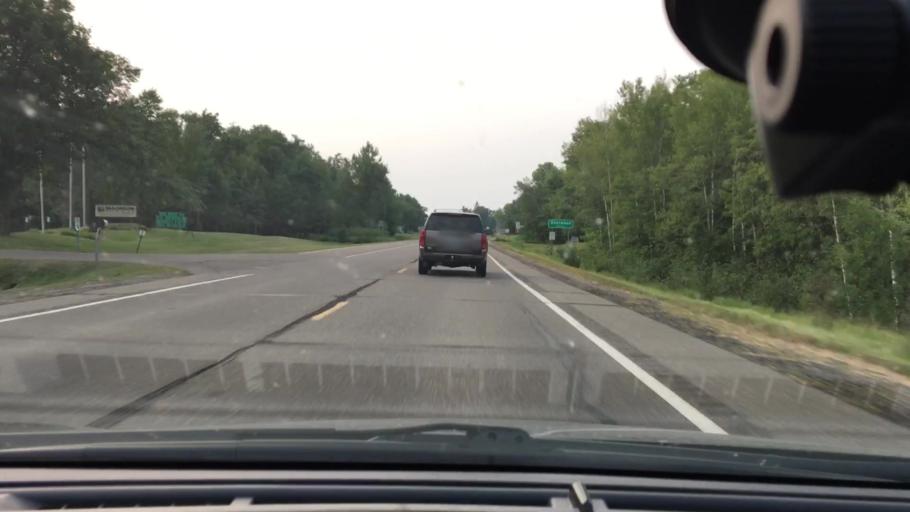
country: US
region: Minnesota
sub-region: Crow Wing County
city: Crosby
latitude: 46.4697
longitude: -93.8882
